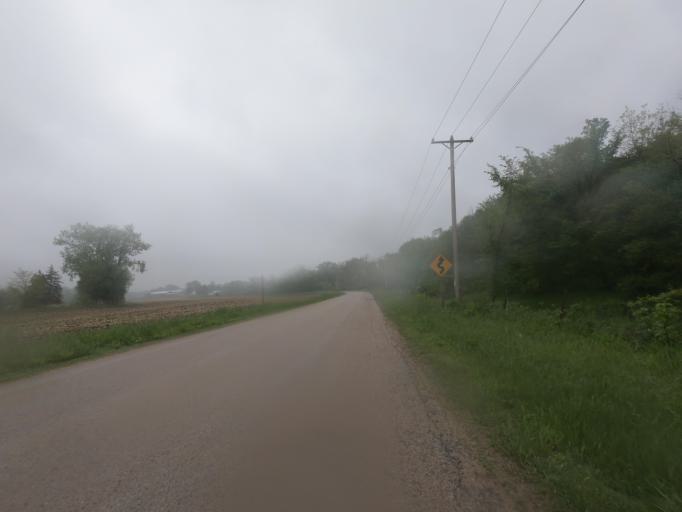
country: US
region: Wisconsin
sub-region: Grant County
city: Hazel Green
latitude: 42.5076
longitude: -90.4776
